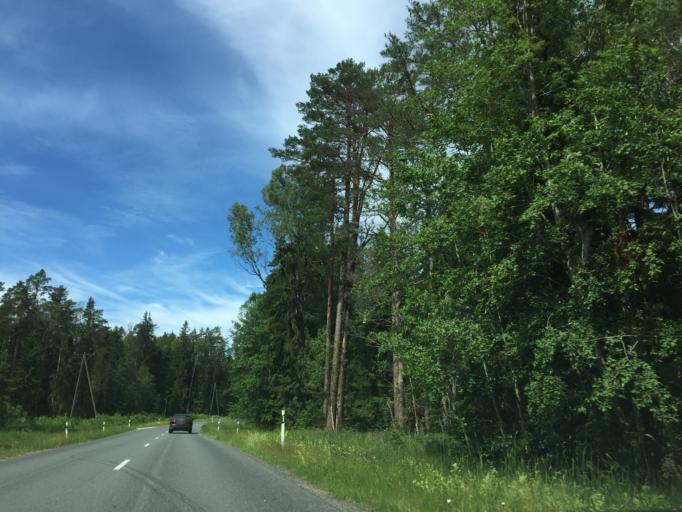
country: LV
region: Dundaga
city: Dundaga
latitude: 57.6348
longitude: 22.5674
